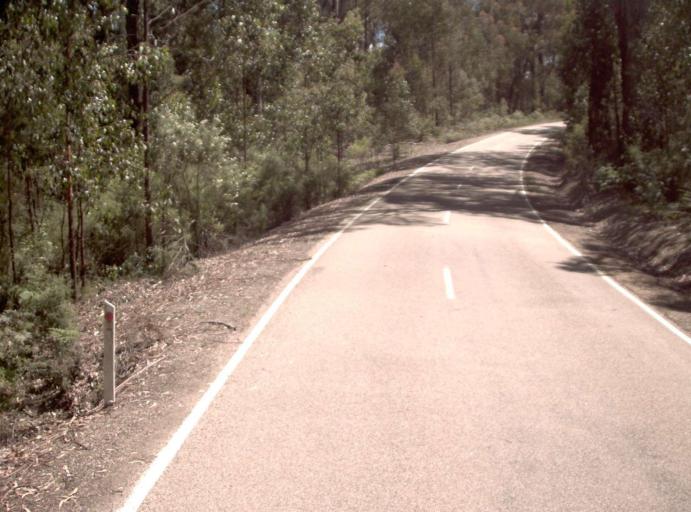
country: AU
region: Victoria
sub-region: East Gippsland
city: Lakes Entrance
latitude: -37.3007
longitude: 148.2463
